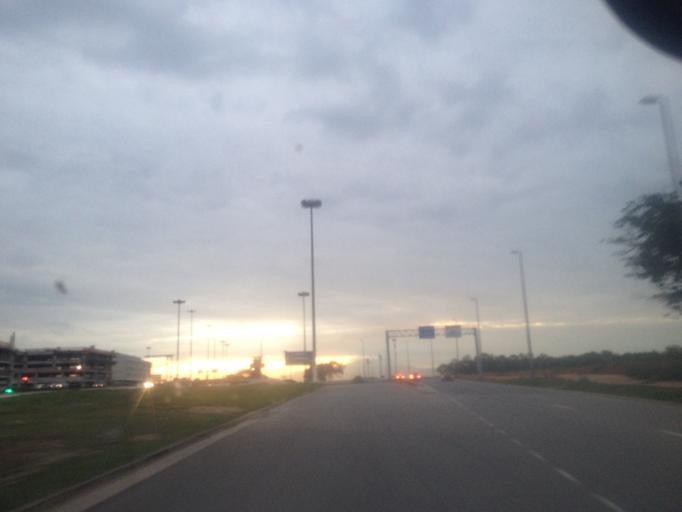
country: BR
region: Rio de Janeiro
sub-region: Duque De Caxias
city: Duque de Caxias
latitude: -22.8143
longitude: -43.2435
